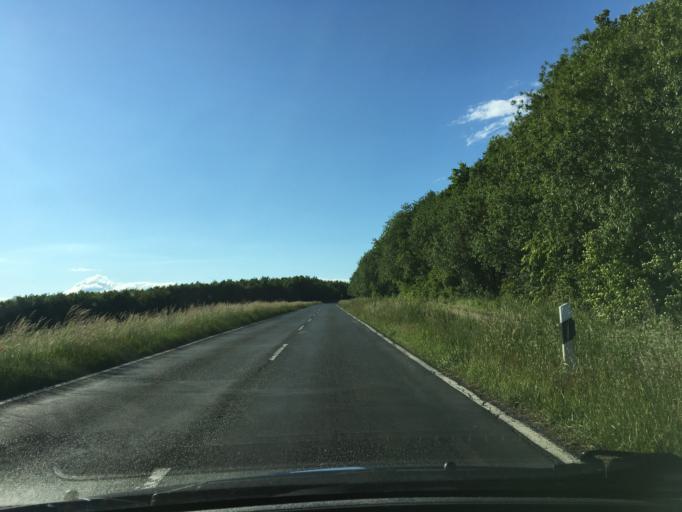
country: DE
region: Lower Saxony
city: Coppengrave
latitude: 51.9936
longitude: 9.7156
